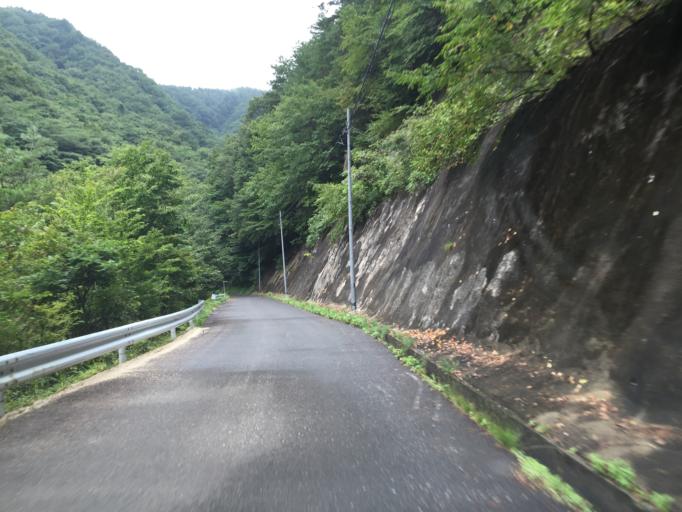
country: JP
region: Fukushima
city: Fukushima-shi
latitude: 37.8026
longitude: 140.3632
